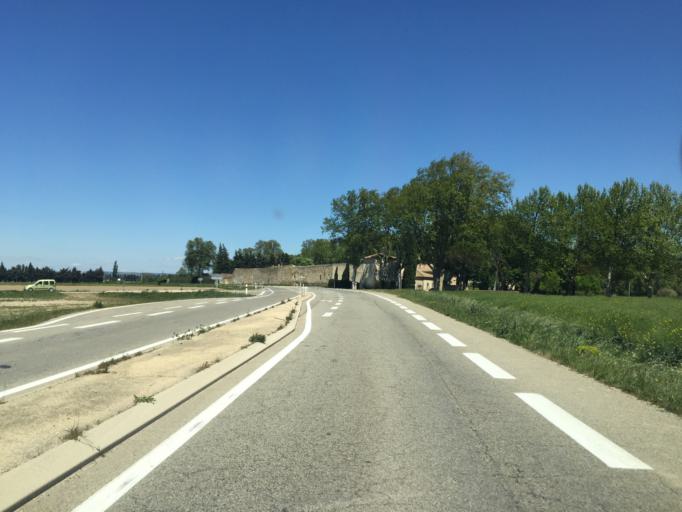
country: FR
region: Provence-Alpes-Cote d'Azur
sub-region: Departement du Vaucluse
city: Jonquieres
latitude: 44.1250
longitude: 4.9331
